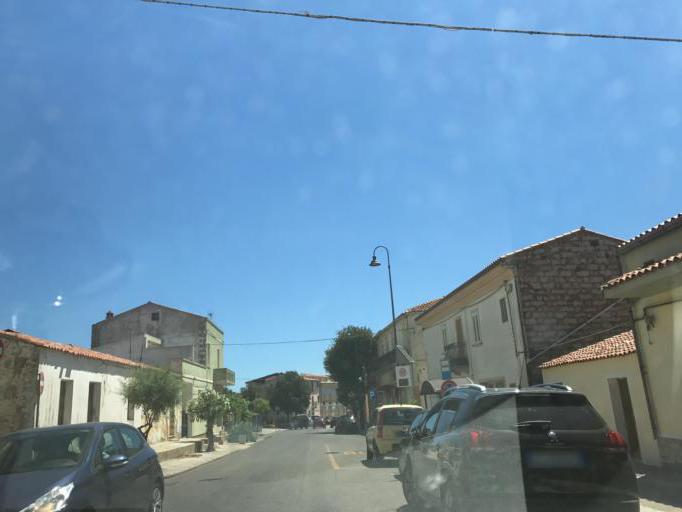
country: IT
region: Sardinia
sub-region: Provincia di Olbia-Tempio
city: Telti
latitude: 40.8759
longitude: 9.3512
